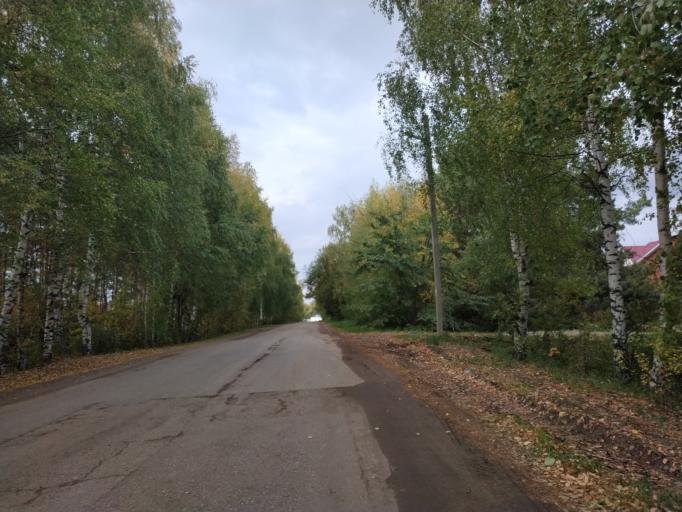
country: RU
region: Chuvashia
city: Ishley
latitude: 56.1292
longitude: 47.0897
